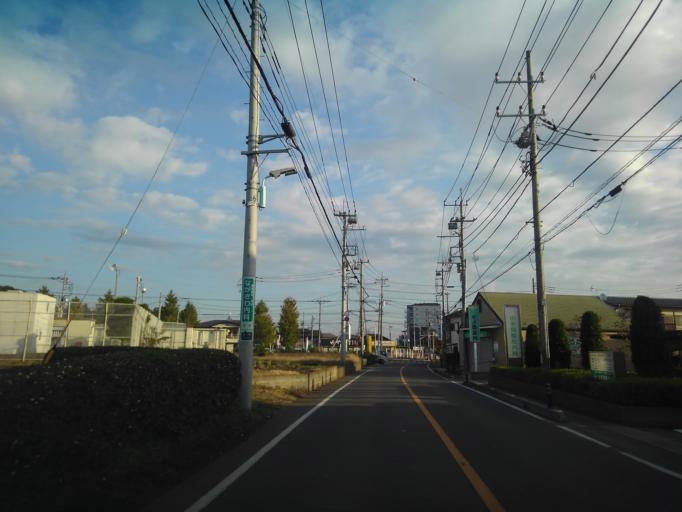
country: JP
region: Saitama
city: Tokorozawa
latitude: 35.7956
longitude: 139.4301
